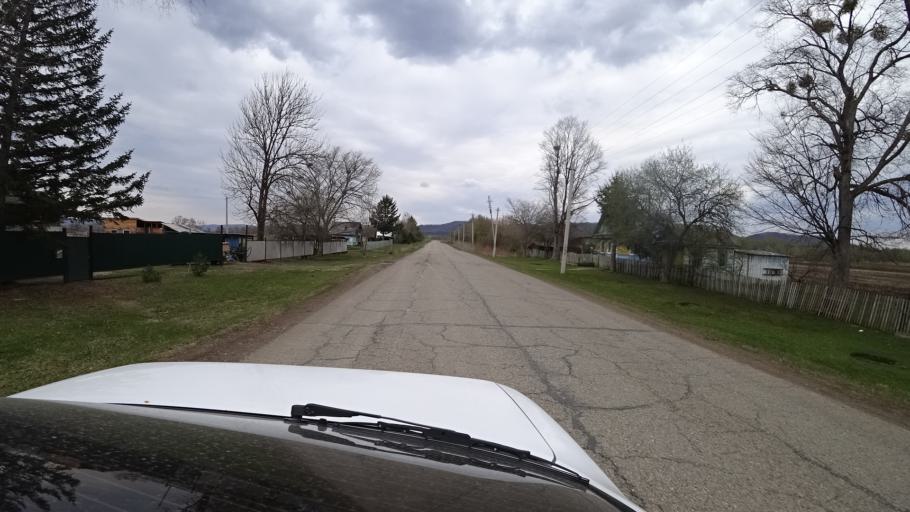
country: RU
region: Primorskiy
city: Novopokrovka
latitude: 45.5514
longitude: 134.3624
